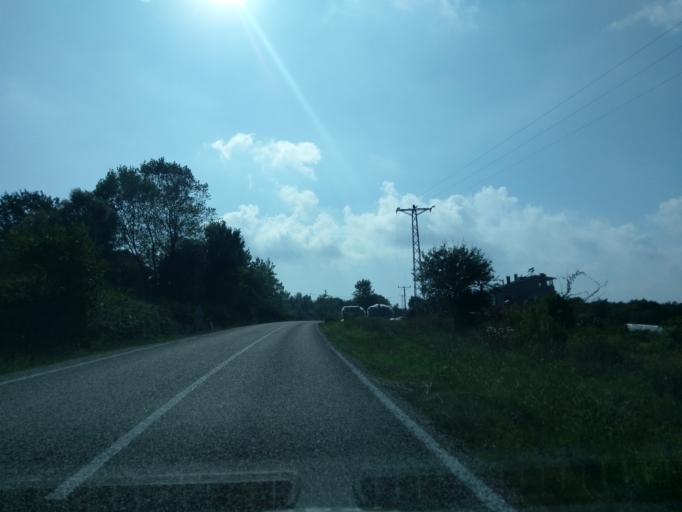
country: TR
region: Sinop
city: Erfelek
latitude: 41.9658
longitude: 34.8534
